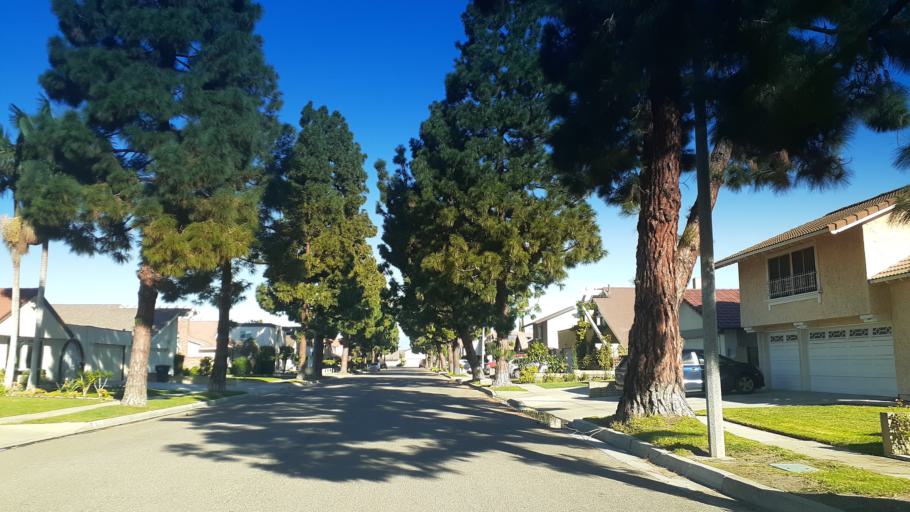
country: US
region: California
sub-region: Los Angeles County
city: Cerritos
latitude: 33.8595
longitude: -118.0661
